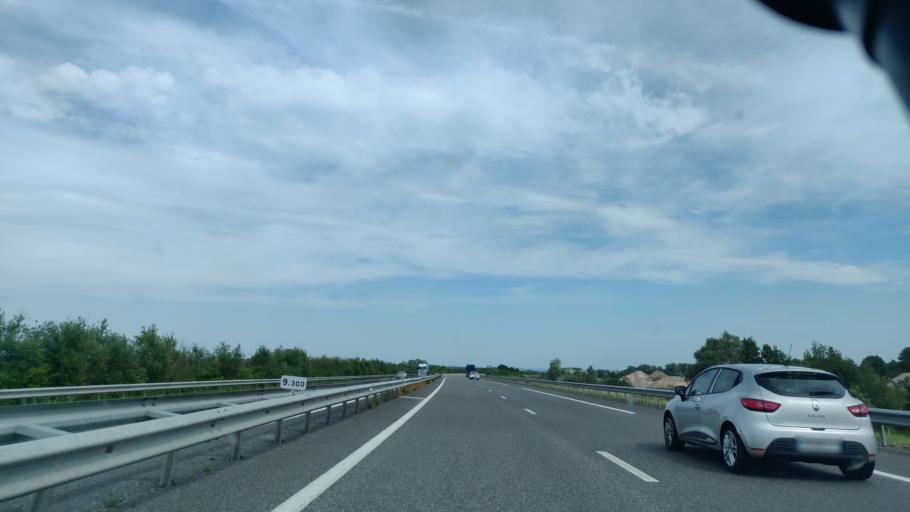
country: FR
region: Lorraine
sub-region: Departement de Meurthe-et-Moselle
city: Gerbeviller
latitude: 48.5307
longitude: 6.5873
